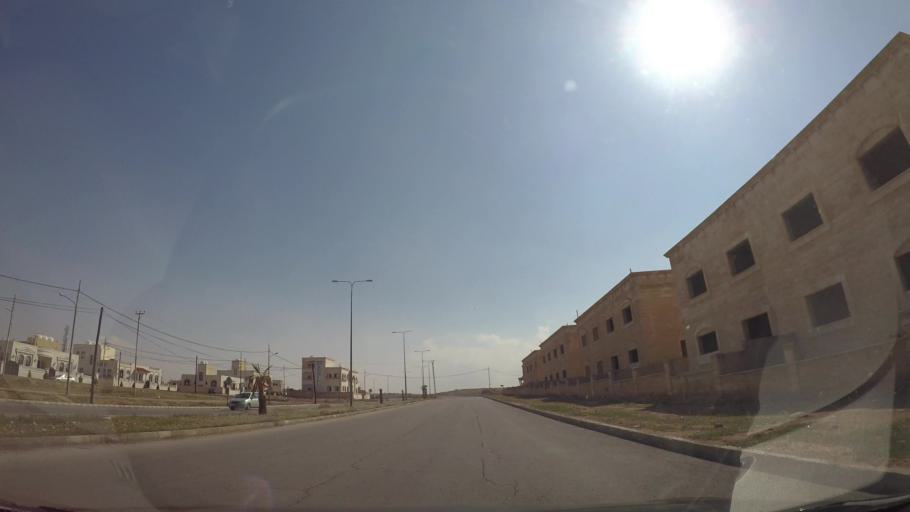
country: JO
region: Zarqa
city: Zarqa
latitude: 32.0617
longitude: 36.1126
